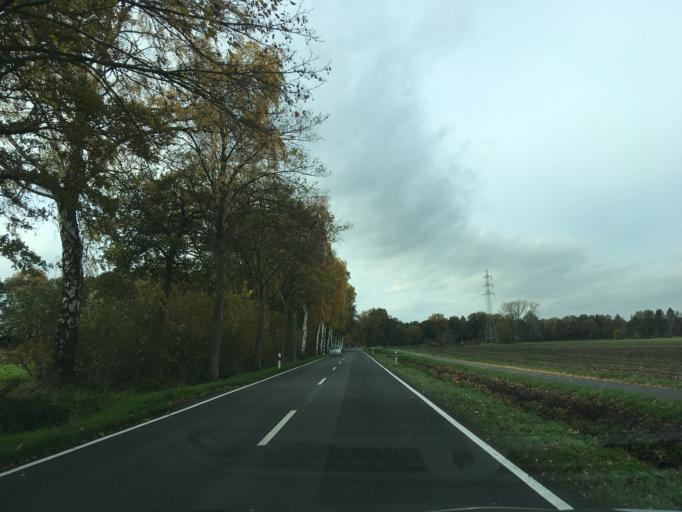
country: DE
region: North Rhine-Westphalia
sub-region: Regierungsbezirk Munster
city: Vreden
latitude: 52.0792
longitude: 6.9039
